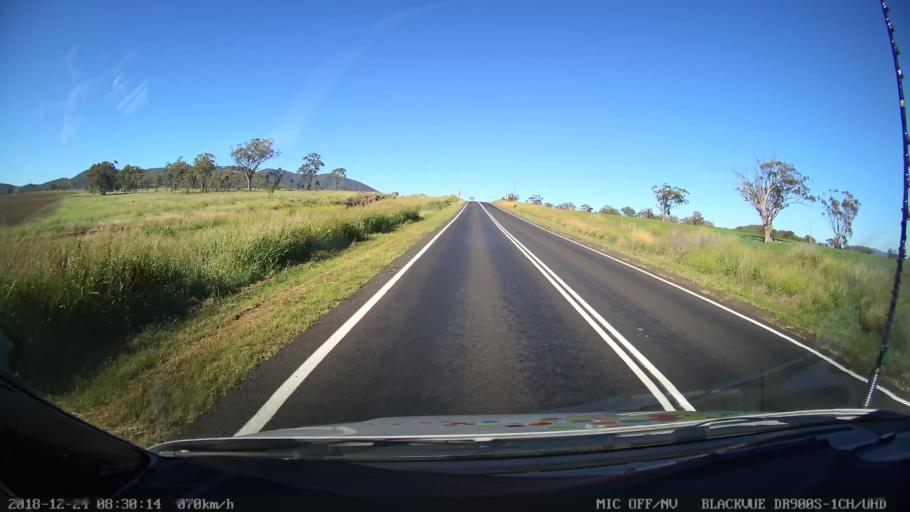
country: AU
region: New South Wales
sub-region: Tamworth Municipality
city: Phillip
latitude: -31.2666
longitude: 150.7267
